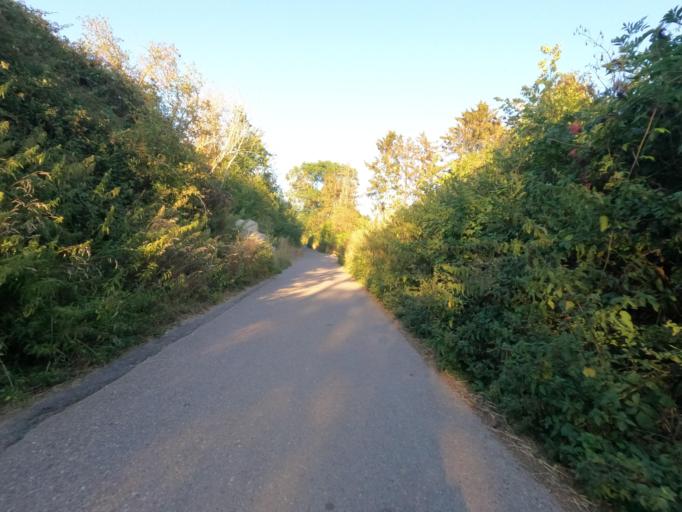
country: DE
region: North Rhine-Westphalia
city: Julich
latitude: 50.9705
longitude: 6.3402
